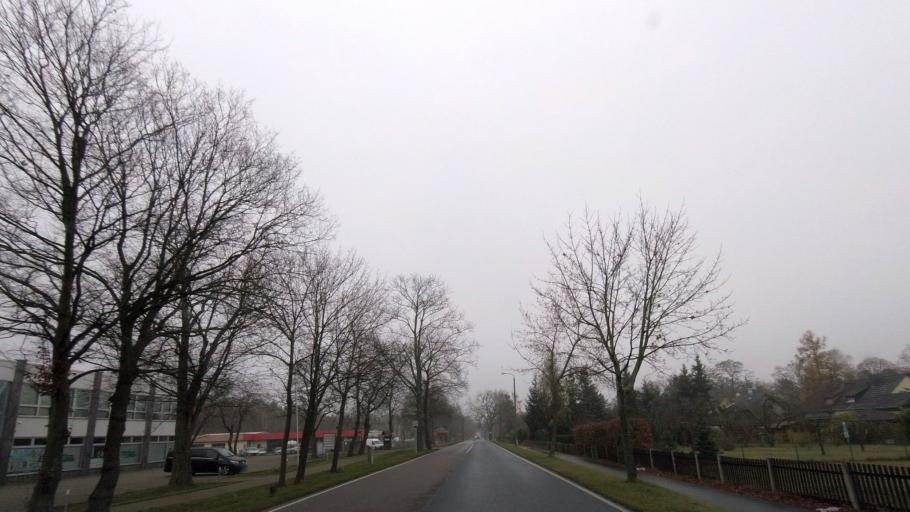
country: DE
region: Brandenburg
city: Niedergorsdorf
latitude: 52.0102
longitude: 13.0084
